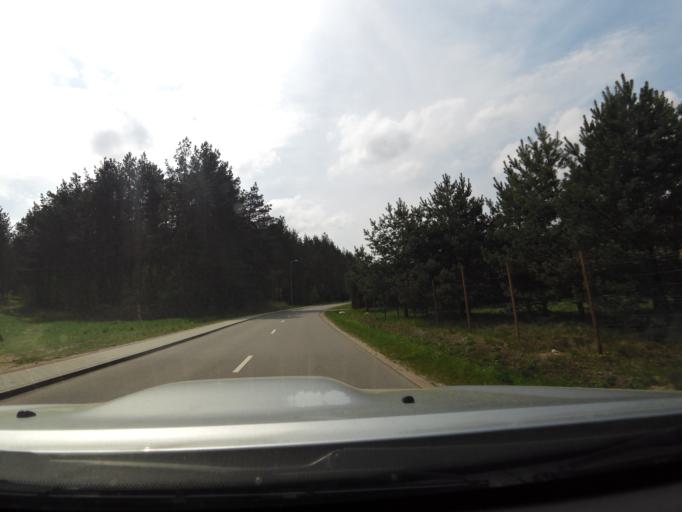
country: LT
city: Salcininkai
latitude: 54.4344
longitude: 25.3246
